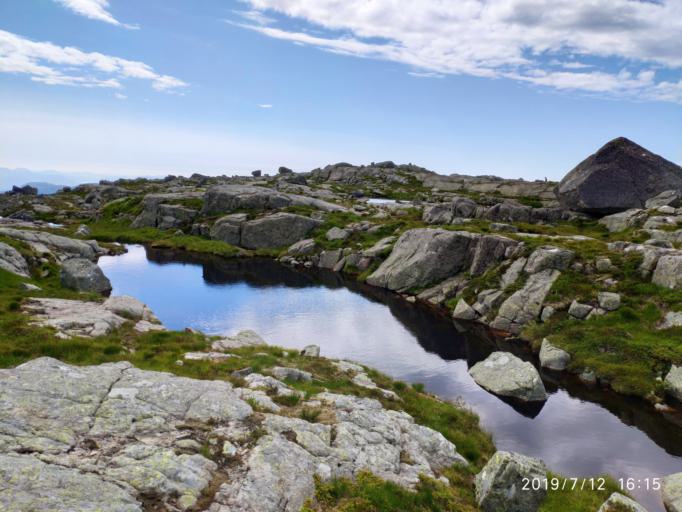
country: NO
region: Rogaland
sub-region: Forsand
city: Forsand
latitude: 58.9845
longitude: 6.1843
